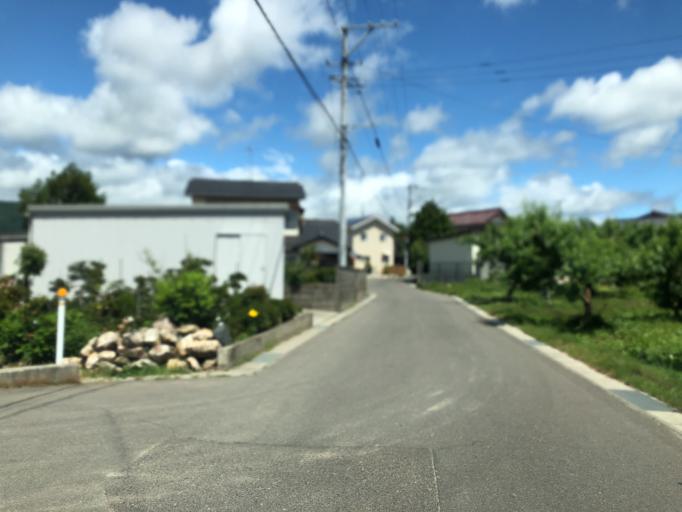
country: JP
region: Fukushima
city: Fukushima-shi
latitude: 37.8024
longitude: 140.4361
